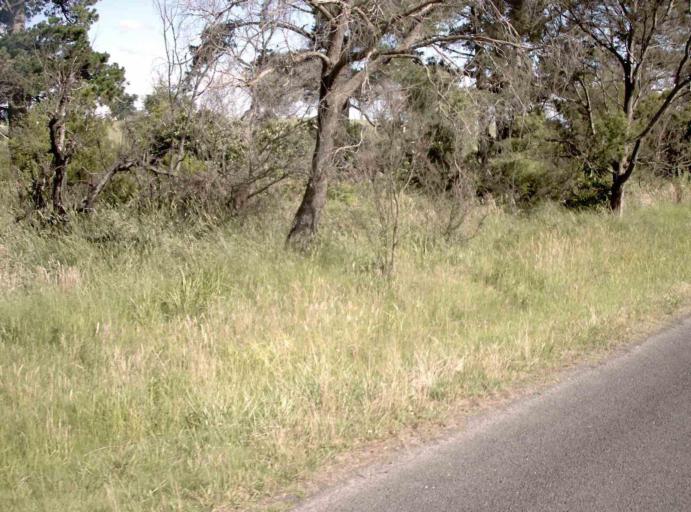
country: AU
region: Victoria
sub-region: Cardinia
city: Koo-Wee-Rup
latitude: -38.2998
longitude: 145.5439
